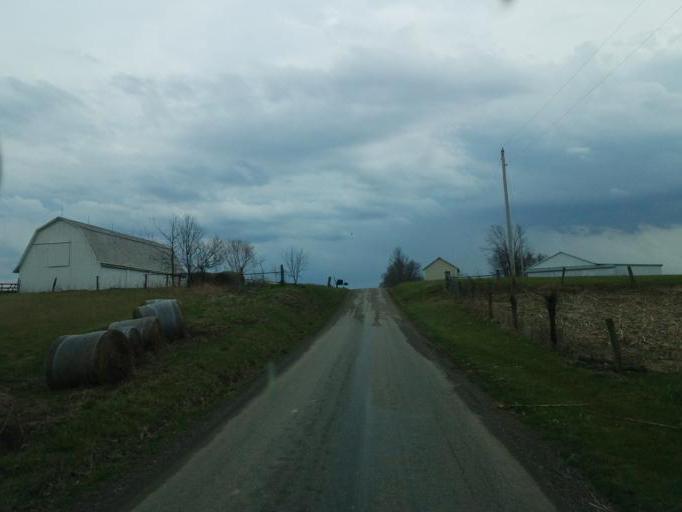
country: US
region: Ohio
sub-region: Muskingum County
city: New Concord
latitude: 40.0784
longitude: -81.8299
